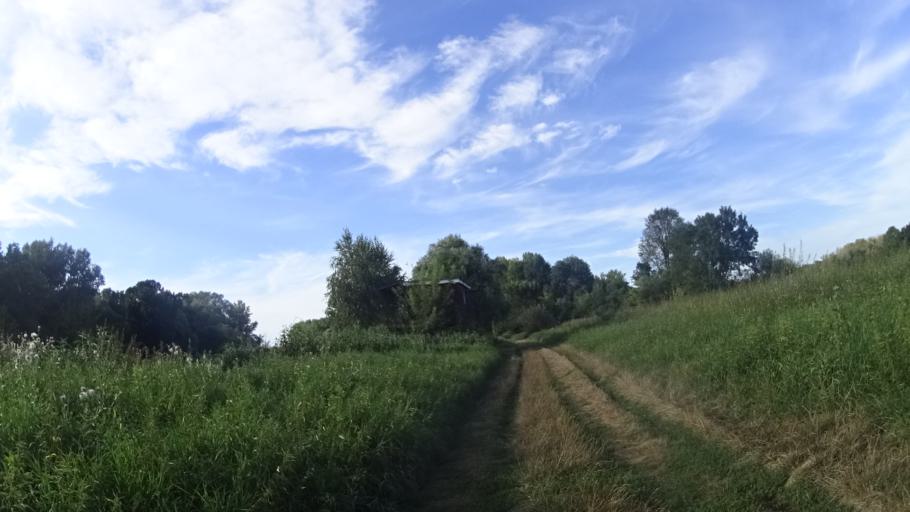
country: AT
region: Lower Austria
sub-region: Politischer Bezirk Mistelbach
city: Rabensburg
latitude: 48.6087
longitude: 16.9428
